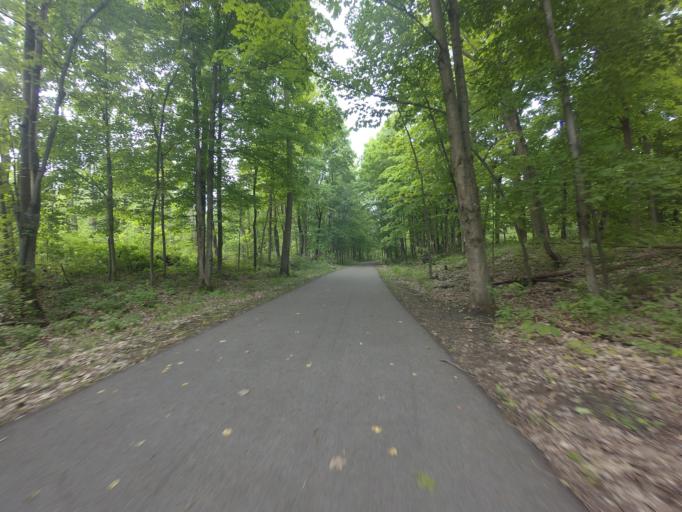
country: US
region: New York
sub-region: Jefferson County
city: Calcium
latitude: 43.9756
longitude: -75.8597
